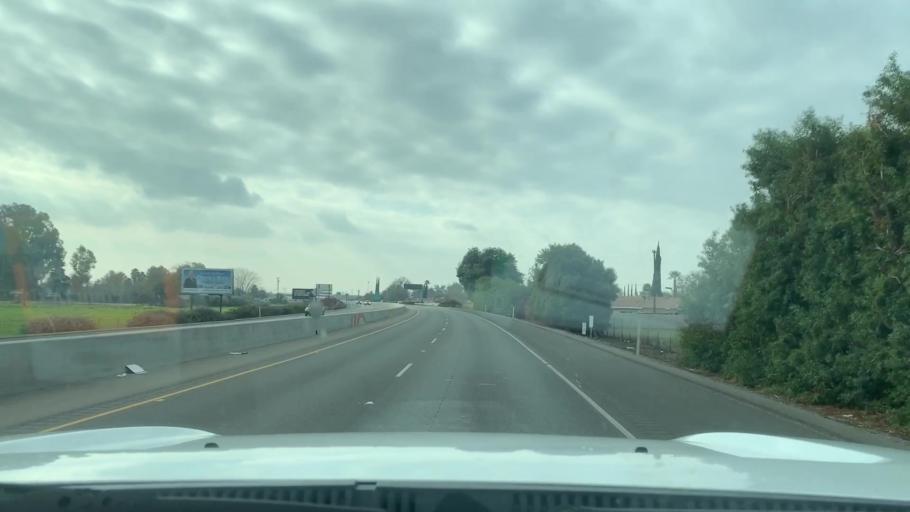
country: US
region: California
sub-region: Kings County
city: Lemoore
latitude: 36.2913
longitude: -119.7866
